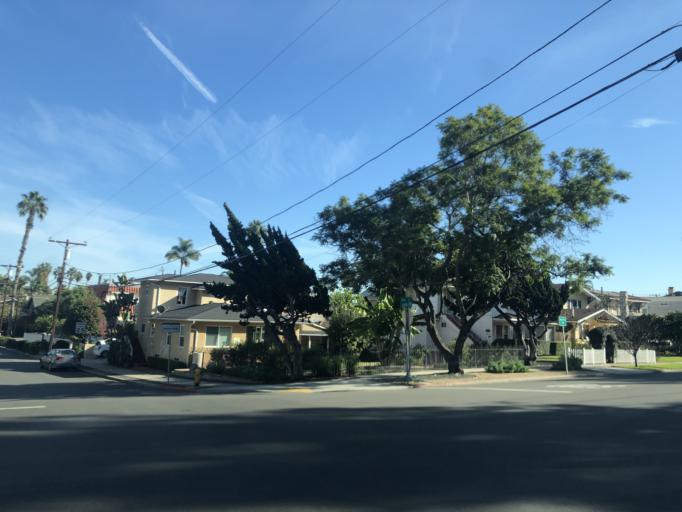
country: US
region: California
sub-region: San Diego County
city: San Diego
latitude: 32.7235
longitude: -117.1340
